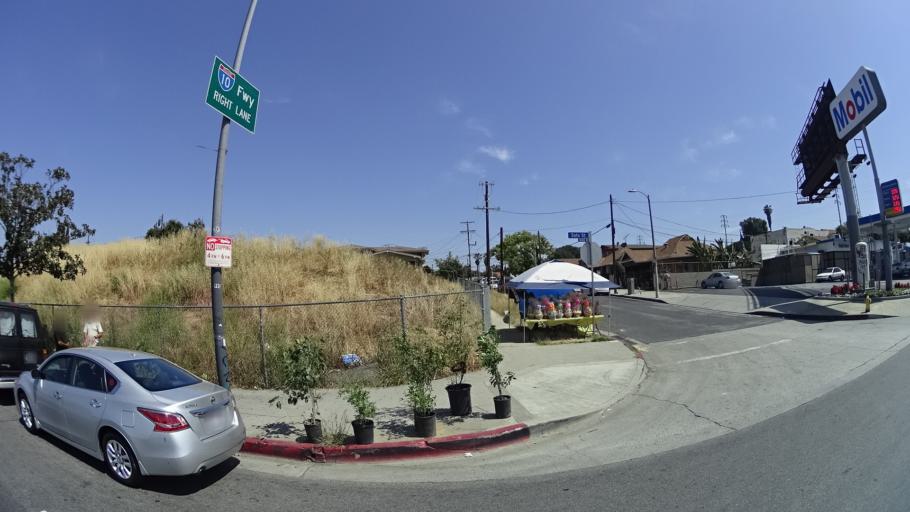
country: US
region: California
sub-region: Los Angeles County
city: Boyle Heights
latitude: 34.0537
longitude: -118.2033
